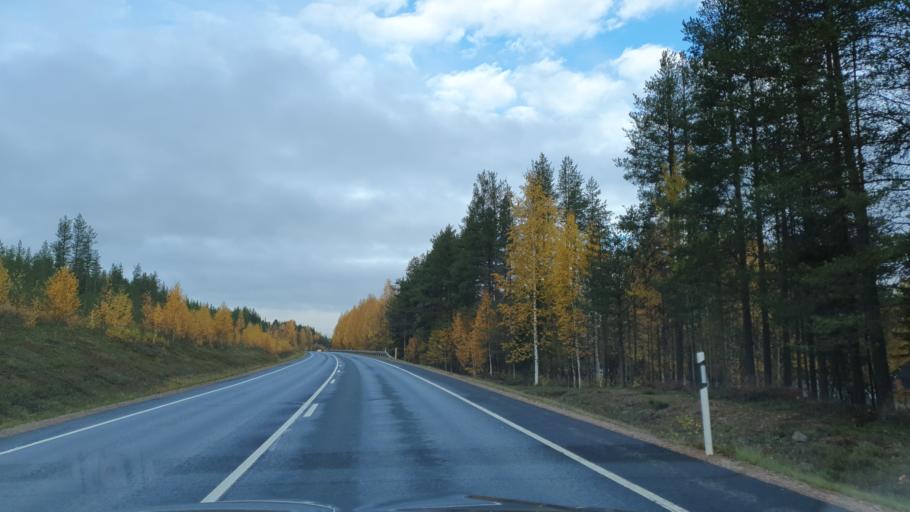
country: FI
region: Lapland
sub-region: Rovaniemi
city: Rovaniemi
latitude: 66.6010
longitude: 25.5894
